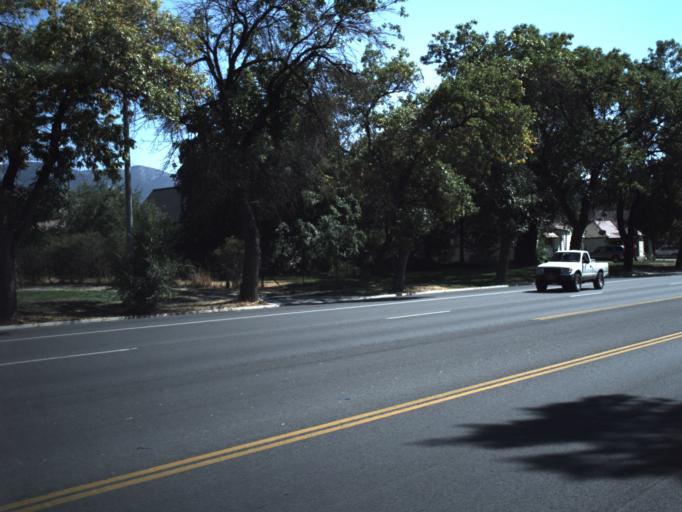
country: US
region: Utah
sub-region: Cache County
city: Smithfield
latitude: 41.8443
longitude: -111.8326
